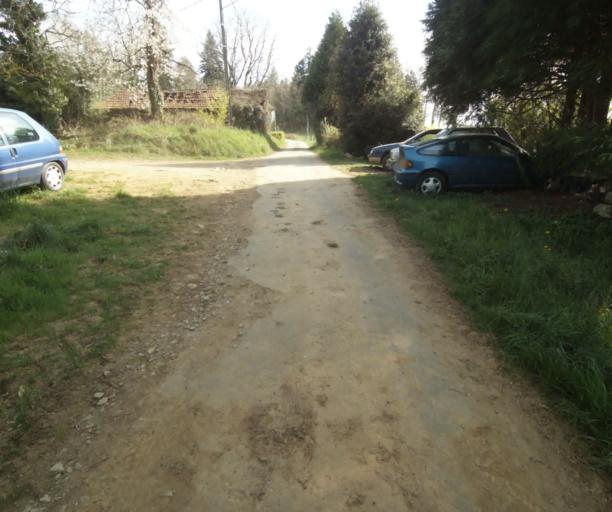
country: FR
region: Limousin
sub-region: Departement de la Correze
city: Naves
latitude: 45.3358
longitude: 1.7646
